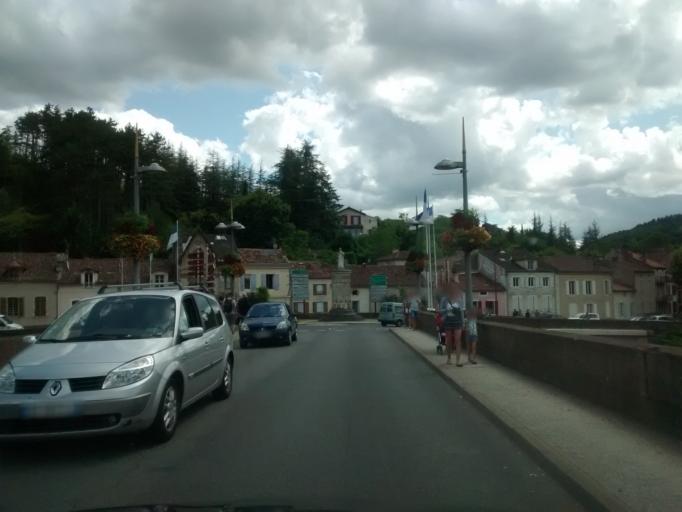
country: FR
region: Midi-Pyrenees
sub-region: Departement du Lot
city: Cahors
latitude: 44.4413
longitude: 1.4428
